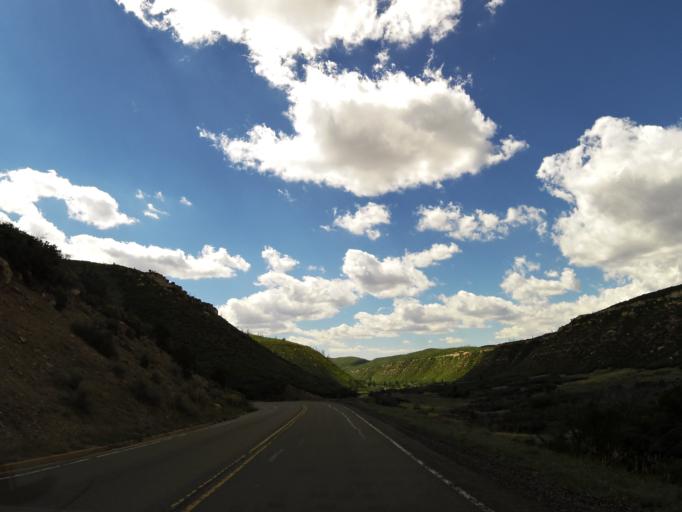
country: US
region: Colorado
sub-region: Montezuma County
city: Mancos
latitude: 37.2958
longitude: -108.4125
